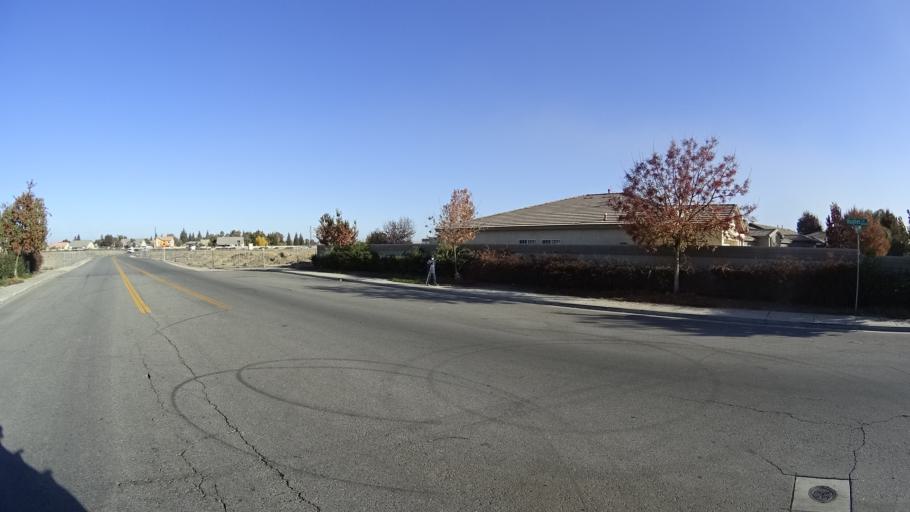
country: US
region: California
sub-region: Kern County
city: Greenfield
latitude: 35.2794
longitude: -119.0306
